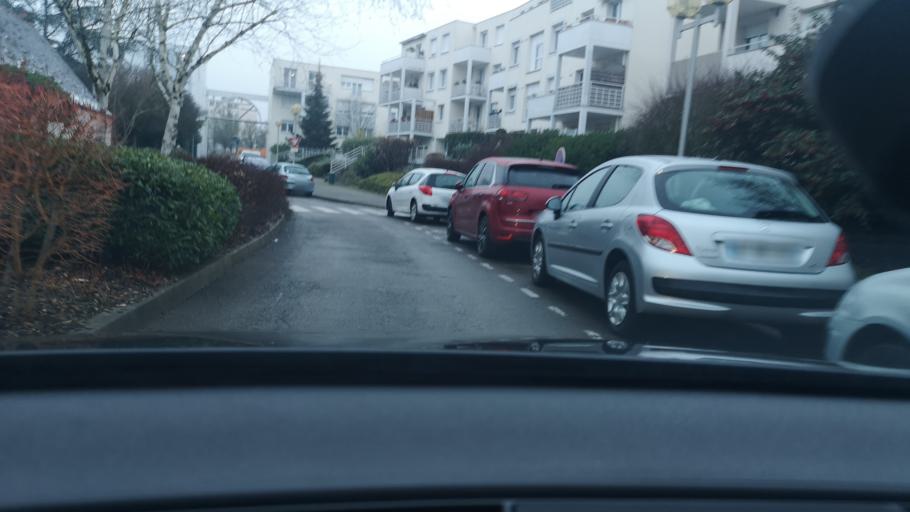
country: FR
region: Bourgogne
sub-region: Departement de la Cote-d'Or
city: Longvic
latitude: 47.2868
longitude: 5.0626
